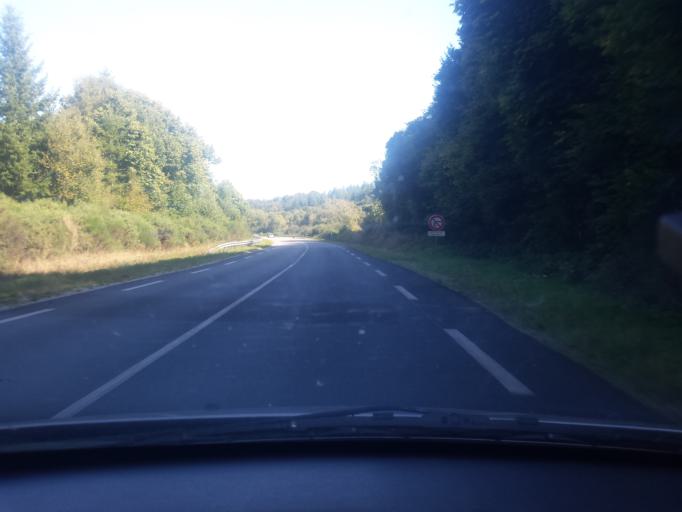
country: FR
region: Brittany
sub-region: Departement du Morbihan
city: Malguenac
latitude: 48.0971
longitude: -3.0485
